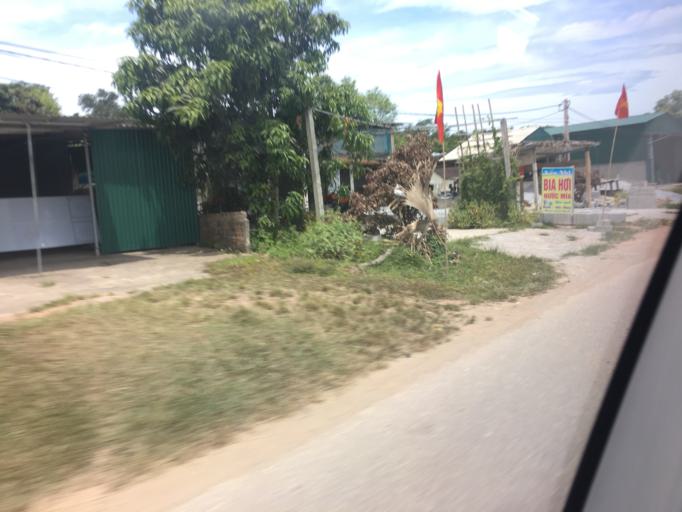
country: VN
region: Ha Tinh
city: Huong Khe
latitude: 18.2639
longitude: 105.6479
